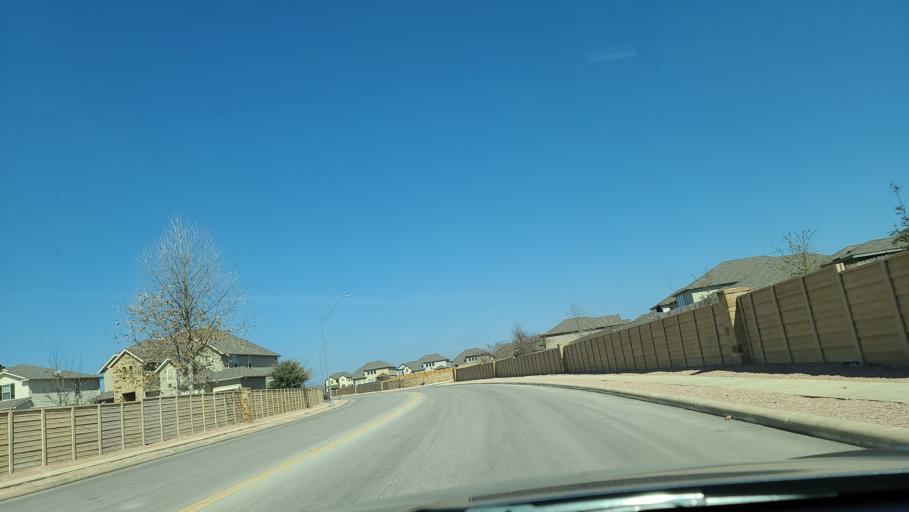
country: US
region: Texas
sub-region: Bexar County
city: Leon Valley
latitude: 29.5584
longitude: -98.6200
